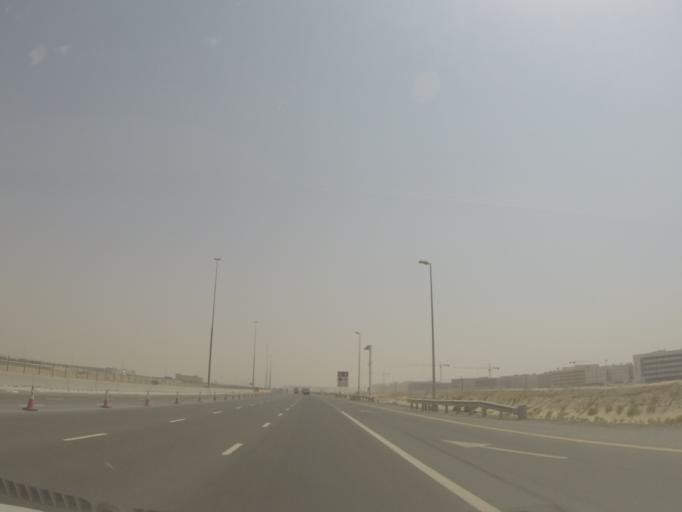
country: AE
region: Dubai
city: Dubai
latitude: 25.0012
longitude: 55.1489
